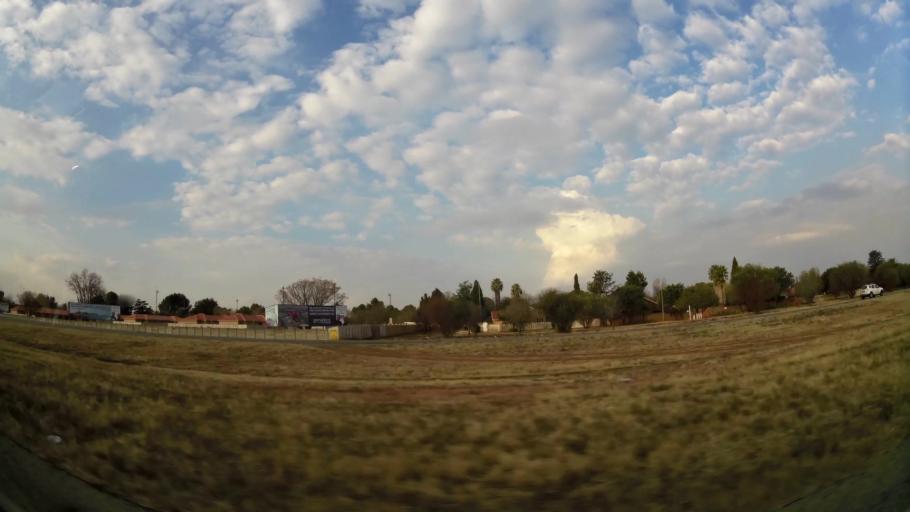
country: ZA
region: Gauteng
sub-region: Sedibeng District Municipality
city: Vanderbijlpark
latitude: -26.7232
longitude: 27.8197
